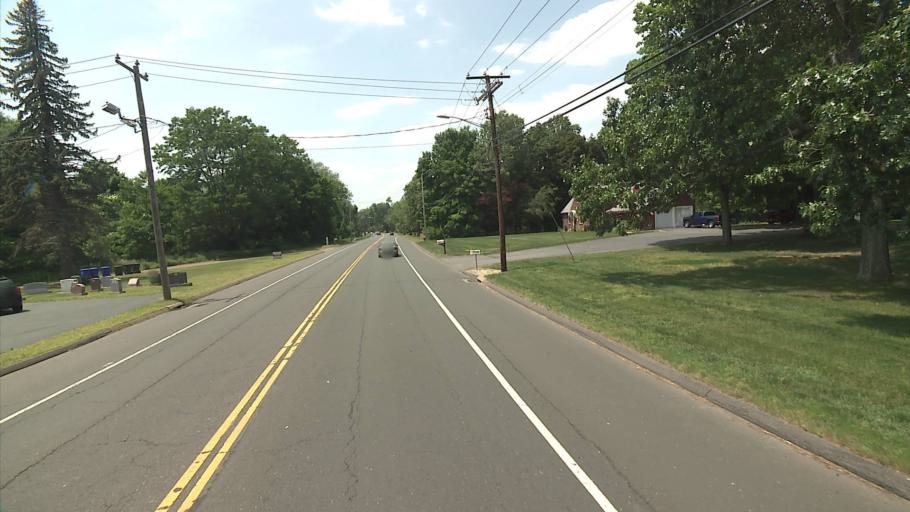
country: US
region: Connecticut
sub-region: Hartford County
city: East Hartford
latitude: 41.7654
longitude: -72.5841
